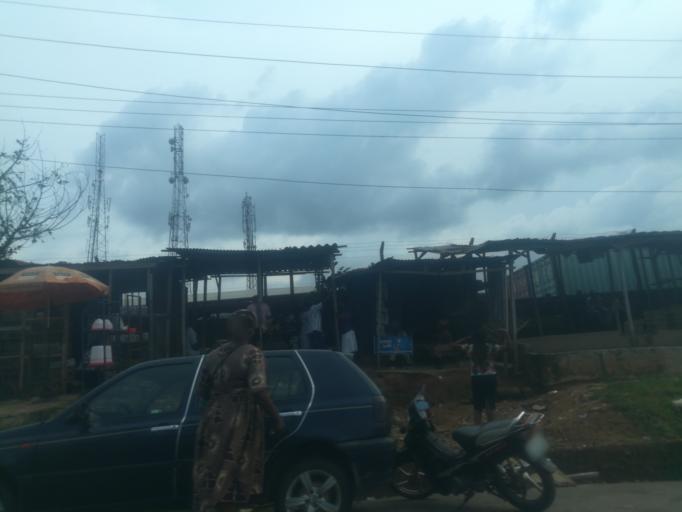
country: NG
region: Oyo
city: Ibadan
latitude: 7.3674
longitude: 3.8529
